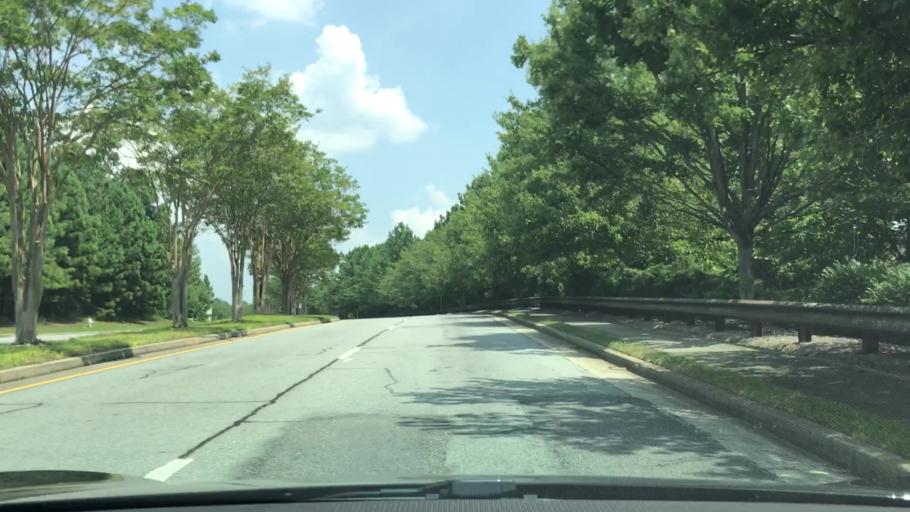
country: US
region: Georgia
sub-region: Gwinnett County
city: Suwanee
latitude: 34.0357
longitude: -84.0624
